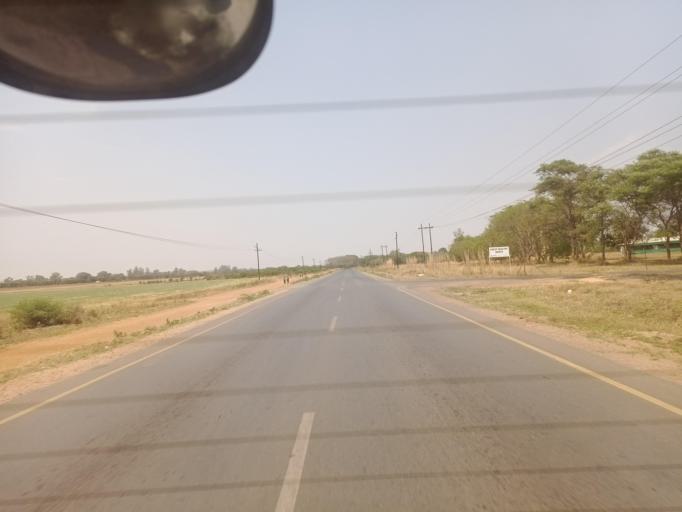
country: ZM
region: Lusaka
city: Lusaka
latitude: -15.2702
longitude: 28.4129
